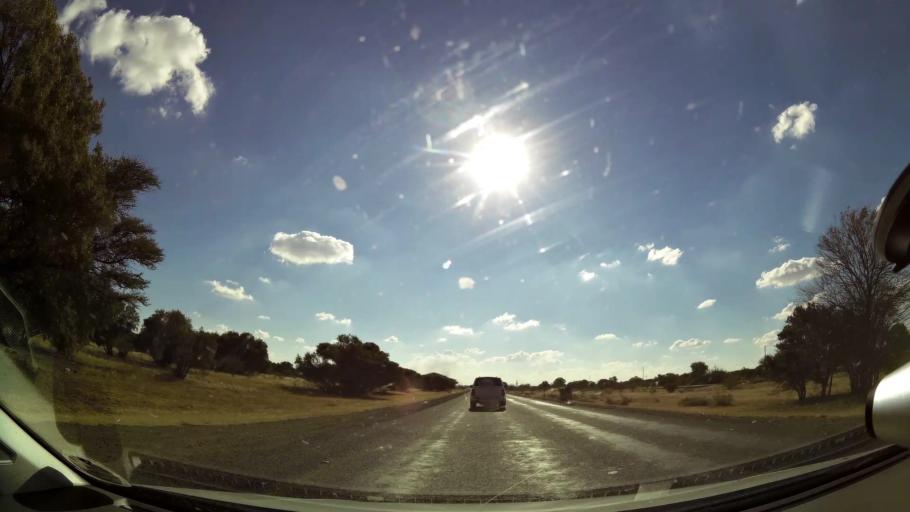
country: ZA
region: Northern Cape
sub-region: Frances Baard District Municipality
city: Kimberley
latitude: -28.7918
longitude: 24.7856
